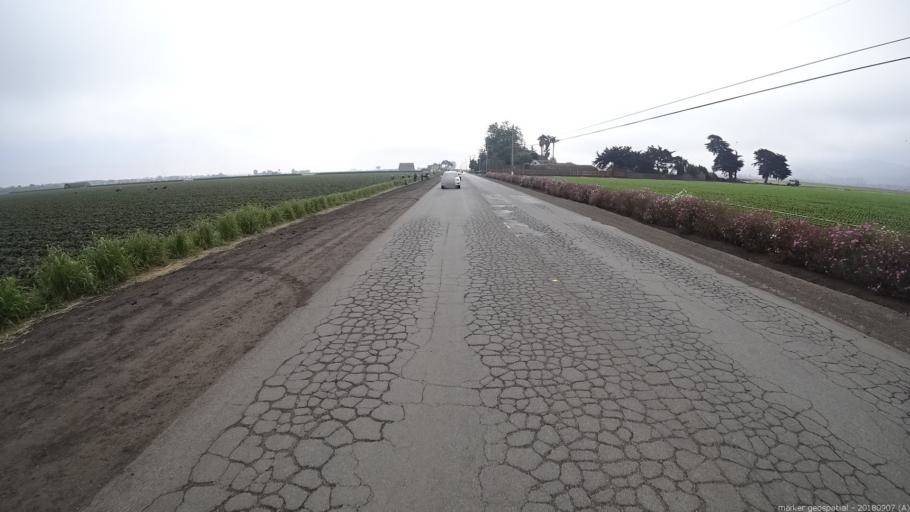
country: US
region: California
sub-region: Monterey County
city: Salinas
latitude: 36.6510
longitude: -121.6768
